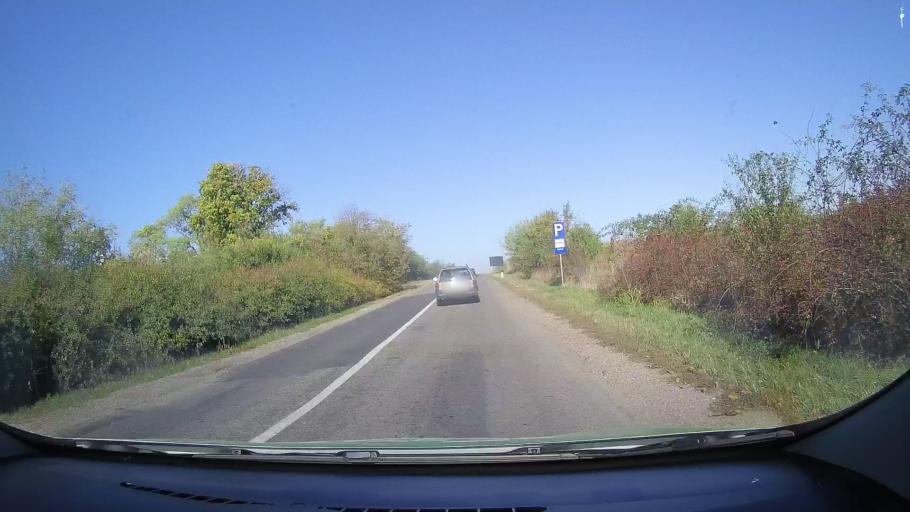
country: RO
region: Satu Mare
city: Carei
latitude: 47.6617
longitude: 22.4936
